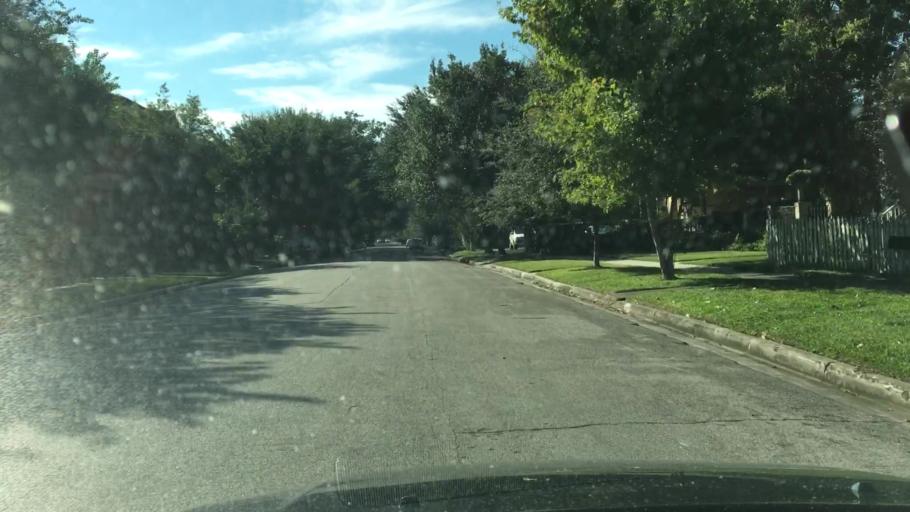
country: US
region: Texas
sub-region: Harris County
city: Houston
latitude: 29.7997
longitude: -95.4014
